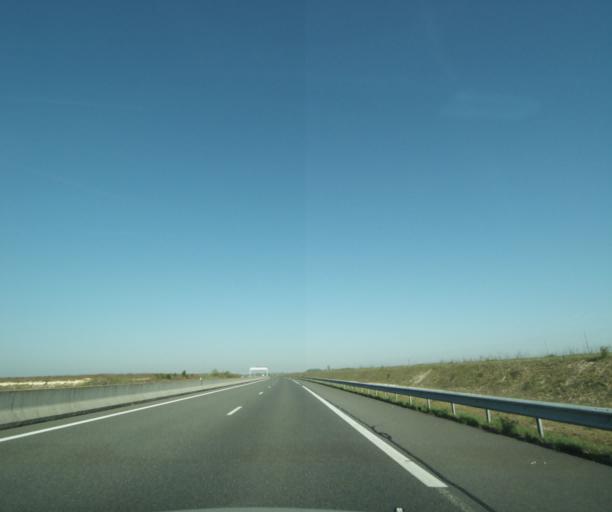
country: FR
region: Centre
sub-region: Departement du Loiret
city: Pannes
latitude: 48.0744
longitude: 2.6362
